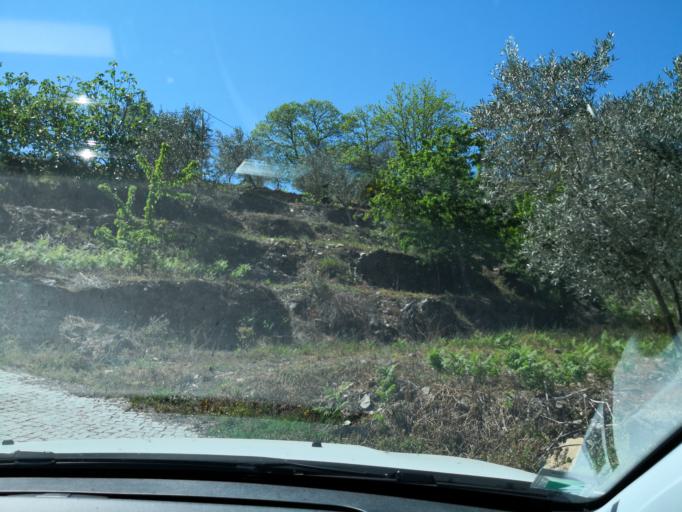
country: PT
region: Vila Real
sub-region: Vila Real
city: Vila Real
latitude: 41.2413
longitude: -7.7201
